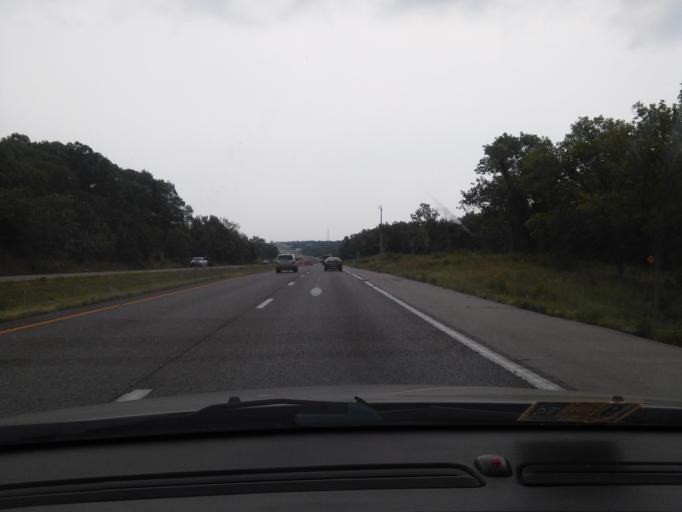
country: US
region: Missouri
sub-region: Boone County
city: Columbia
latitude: 38.9563
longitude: -92.1639
